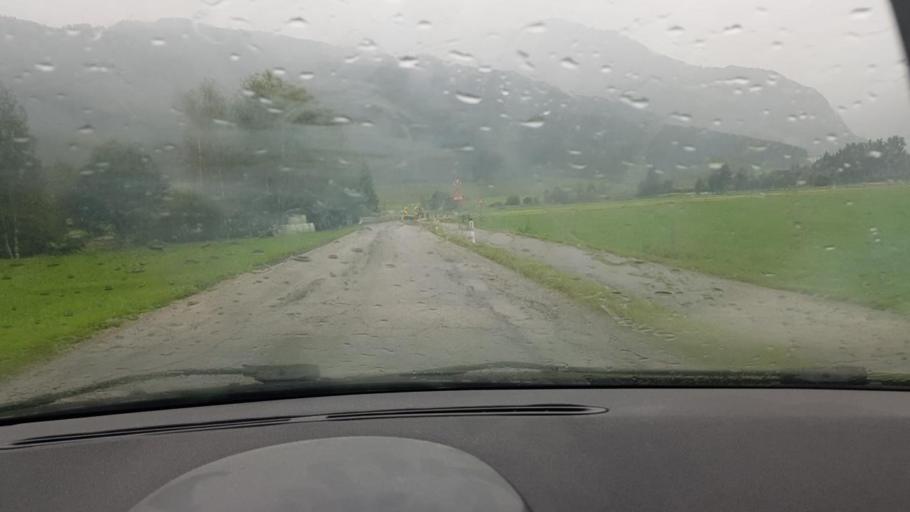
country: AT
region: Salzburg
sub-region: Politischer Bezirk Zell am See
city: Kaprun
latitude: 47.2870
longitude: 12.7847
